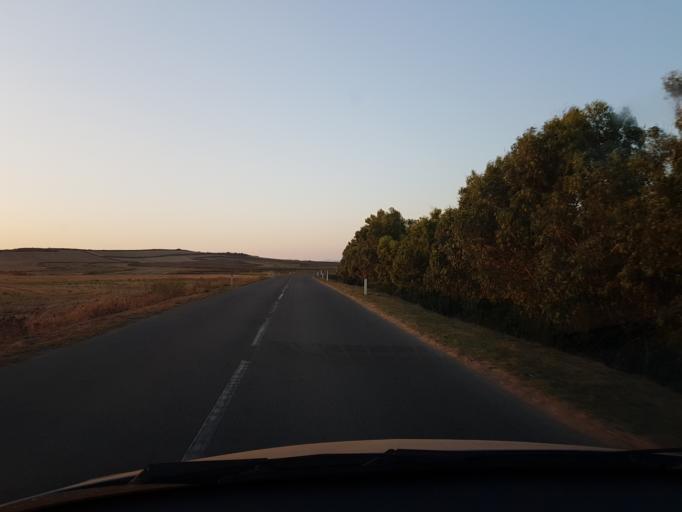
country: IT
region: Sardinia
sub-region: Provincia di Oristano
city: Nurachi
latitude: 39.9729
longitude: 8.4526
